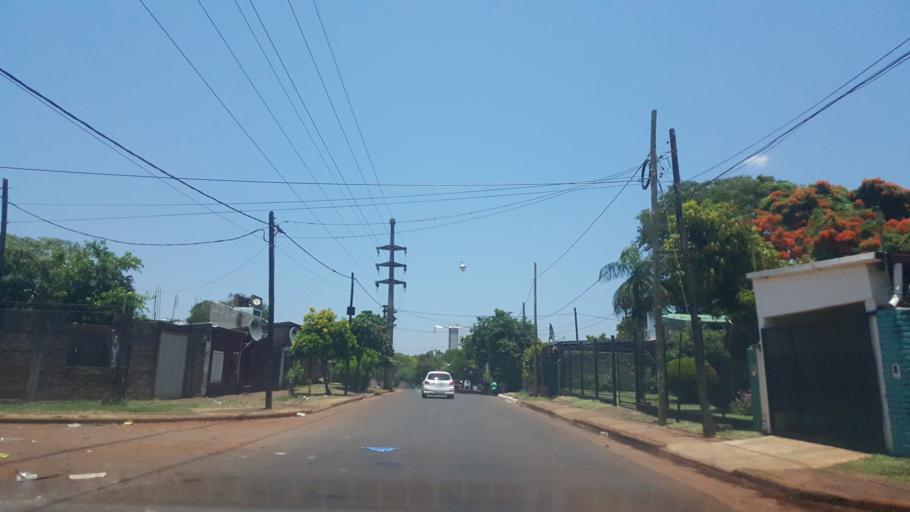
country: AR
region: Misiones
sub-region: Departamento de Capital
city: Posadas
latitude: -27.4008
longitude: -55.8949
